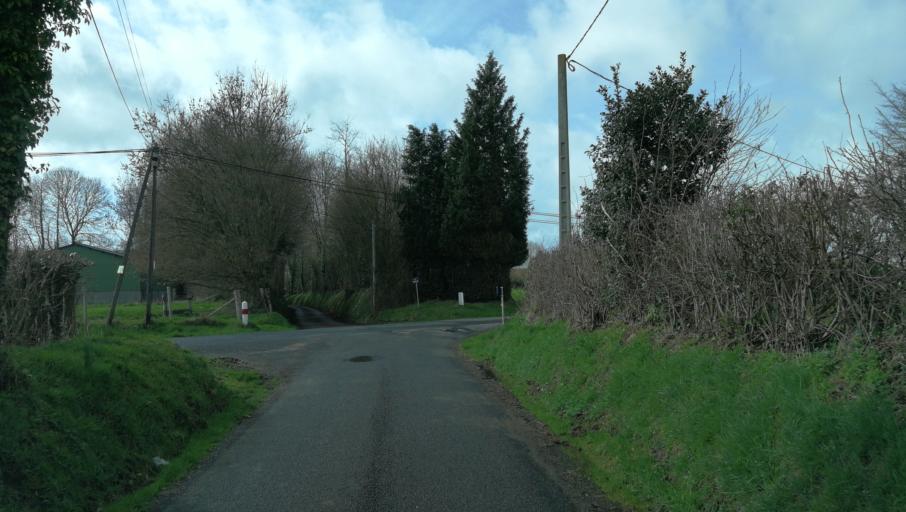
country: FR
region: Haute-Normandie
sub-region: Departement de l'Eure
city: Lieurey
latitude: 49.2389
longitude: 0.4807
